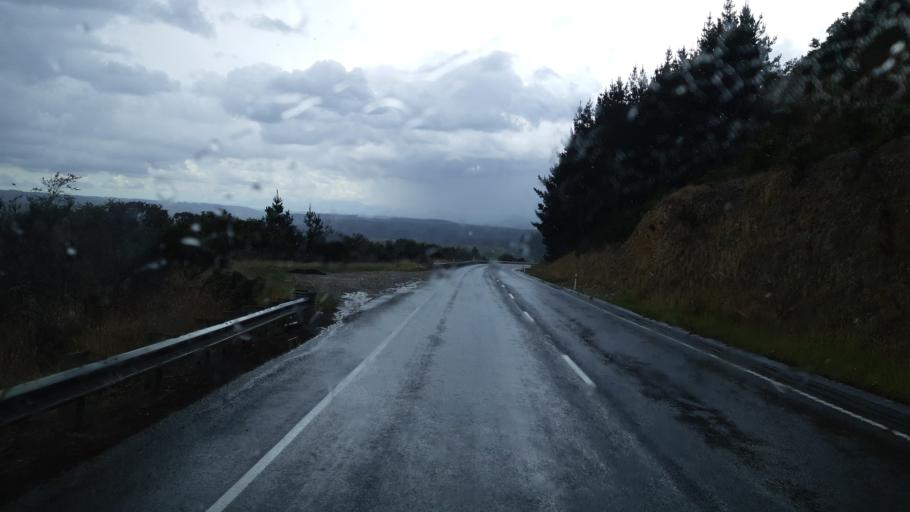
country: NZ
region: Tasman
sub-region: Tasman District
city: Wakefield
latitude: -41.4796
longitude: 172.9181
